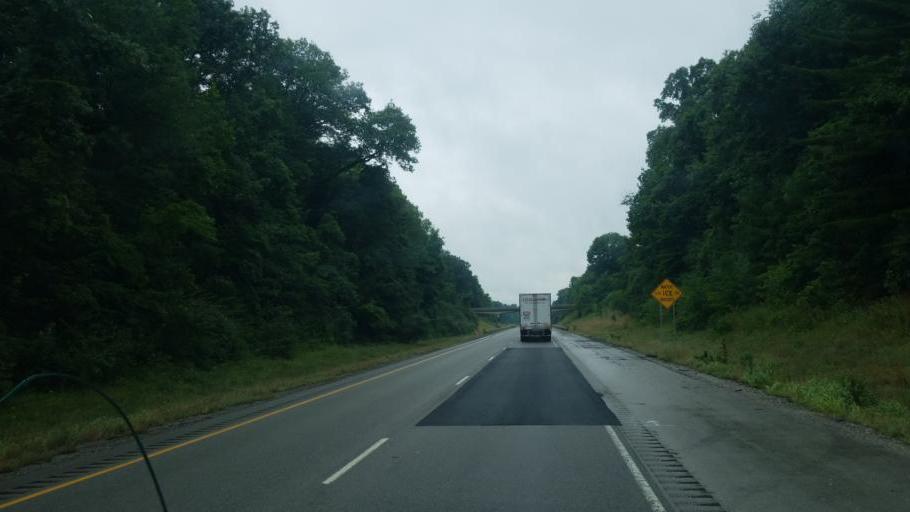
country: US
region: Indiana
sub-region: Putnam County
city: Cloverdale
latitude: 39.5192
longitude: -86.9050
